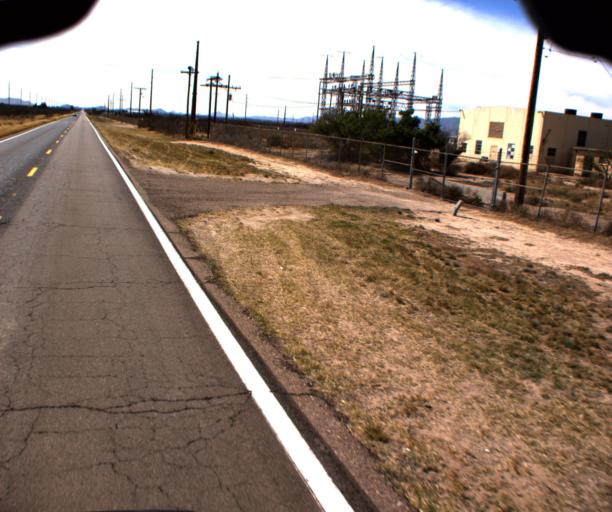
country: US
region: Arizona
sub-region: Cochise County
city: Willcox
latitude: 32.0591
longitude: -109.8906
